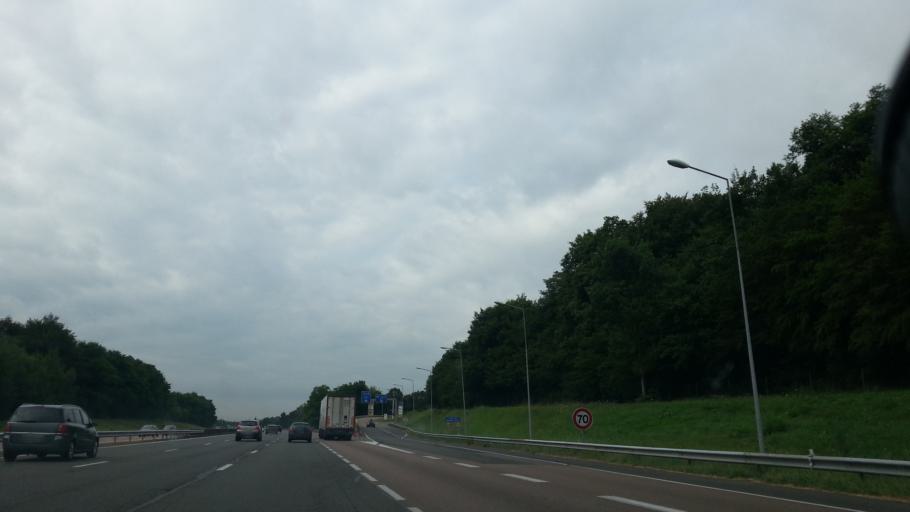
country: FR
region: Bourgogne
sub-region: Departement de la Cote-d'Or
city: Bligny-les-Beaune
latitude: 46.9710
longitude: 4.8400
